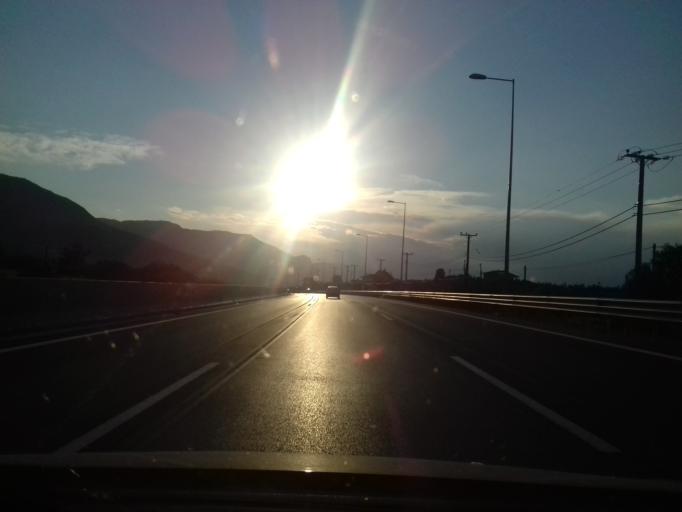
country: GR
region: West Greece
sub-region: Nomos Achaias
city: Akrata
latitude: 38.1714
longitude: 22.2949
